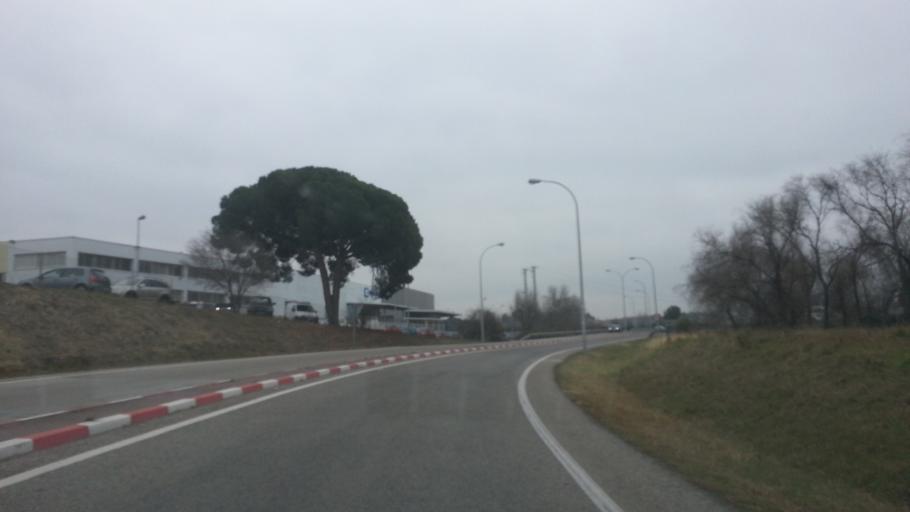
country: ES
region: Catalonia
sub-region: Provincia de Barcelona
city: Terrassa
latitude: 41.5452
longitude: 2.0417
